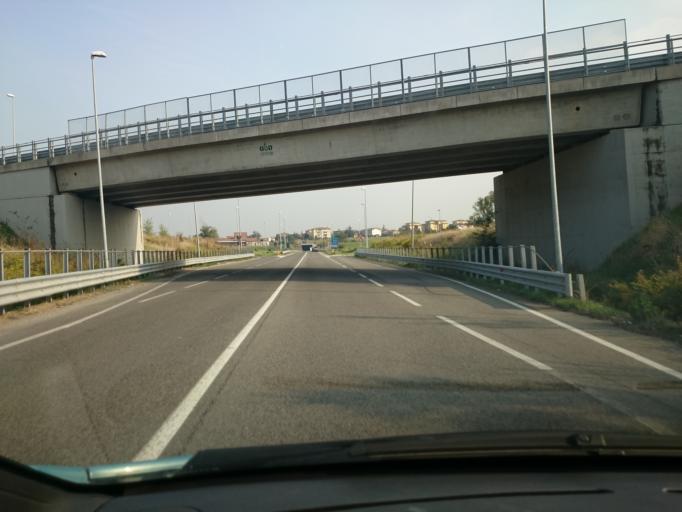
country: IT
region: Emilia-Romagna
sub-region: Provincia di Reggio Emilia
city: Casalgrande
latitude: 44.5860
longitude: 10.7253
